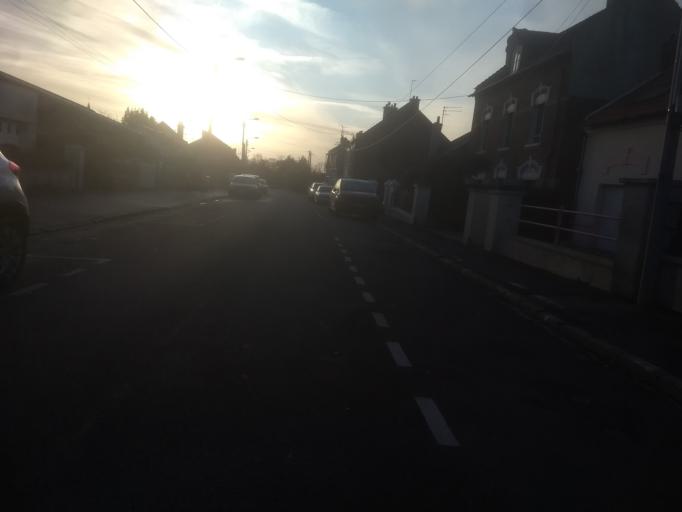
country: FR
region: Nord-Pas-de-Calais
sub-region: Departement du Pas-de-Calais
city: Beaurains
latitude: 50.2651
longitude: 2.7905
